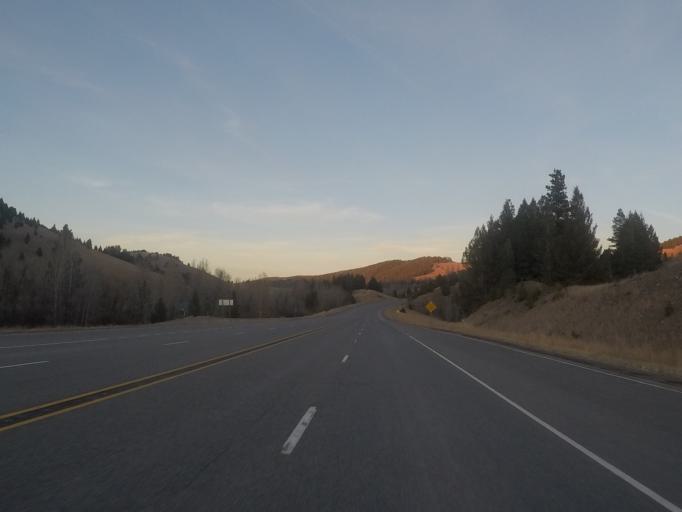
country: US
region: Montana
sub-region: Lewis and Clark County
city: Helena West Side
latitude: 46.5594
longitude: -112.3875
